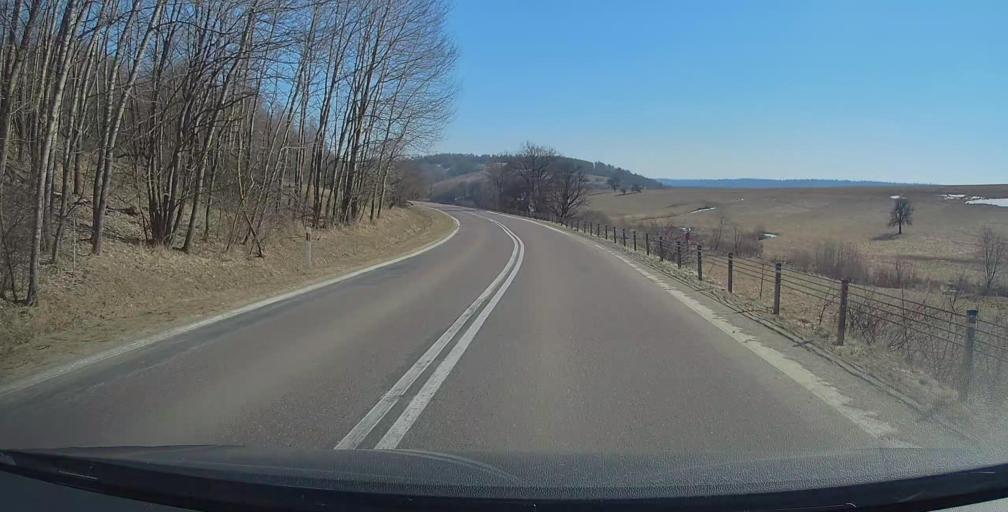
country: PL
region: Subcarpathian Voivodeship
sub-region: Powiat przemyski
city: Bircza
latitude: 49.5966
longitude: 22.4918
